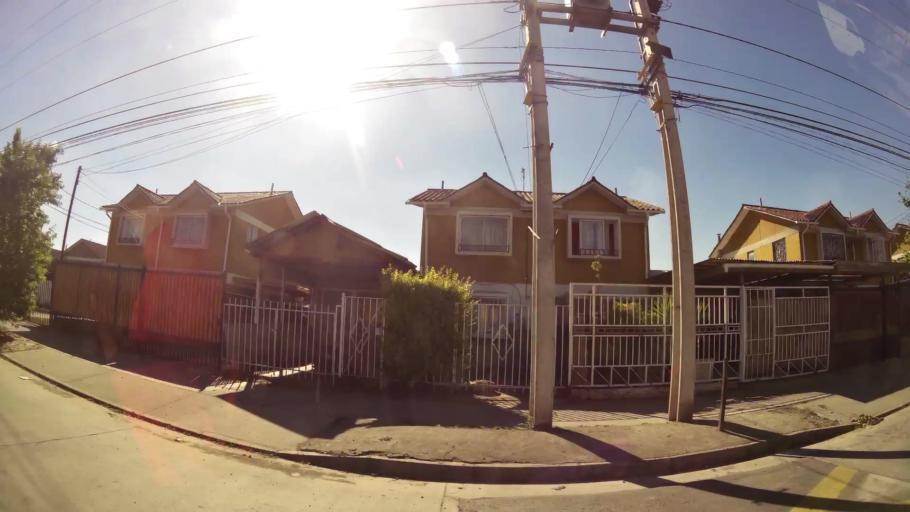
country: CL
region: Santiago Metropolitan
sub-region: Provincia de Maipo
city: San Bernardo
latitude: -33.5504
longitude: -70.7666
